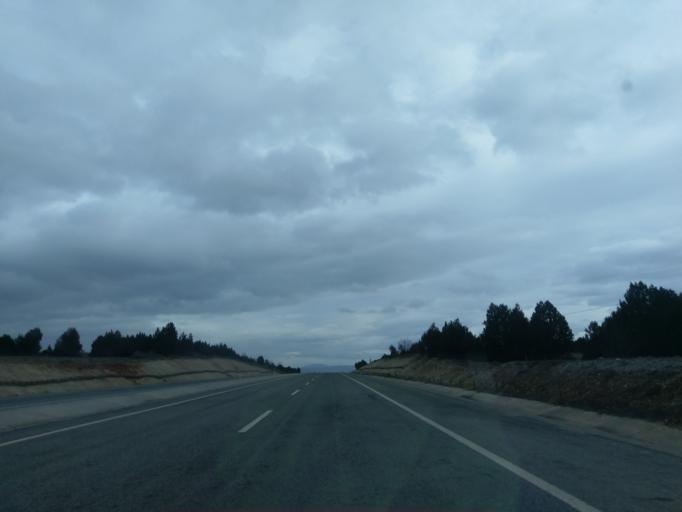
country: TR
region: Kuetahya
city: Aslanapa
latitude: 39.2265
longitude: 29.7581
